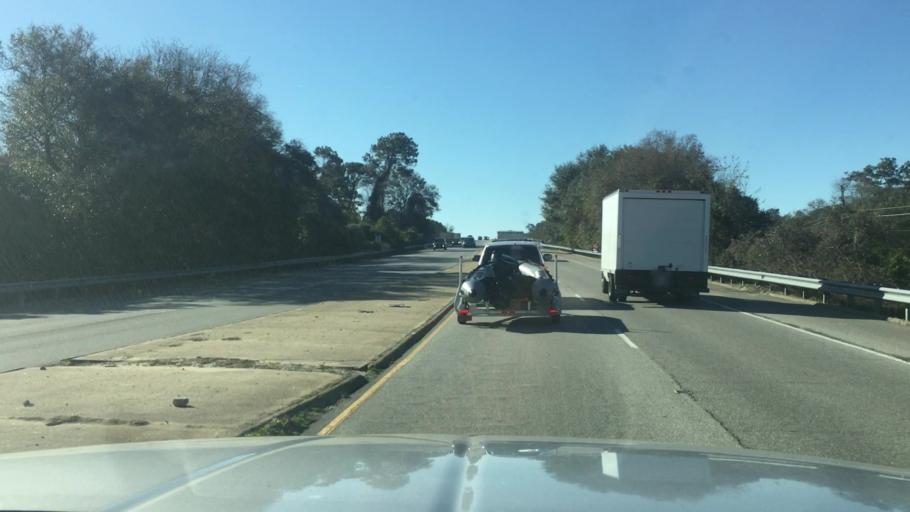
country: US
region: North Carolina
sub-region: New Hanover County
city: Sea Breeze
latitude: 34.0604
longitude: -77.8995
